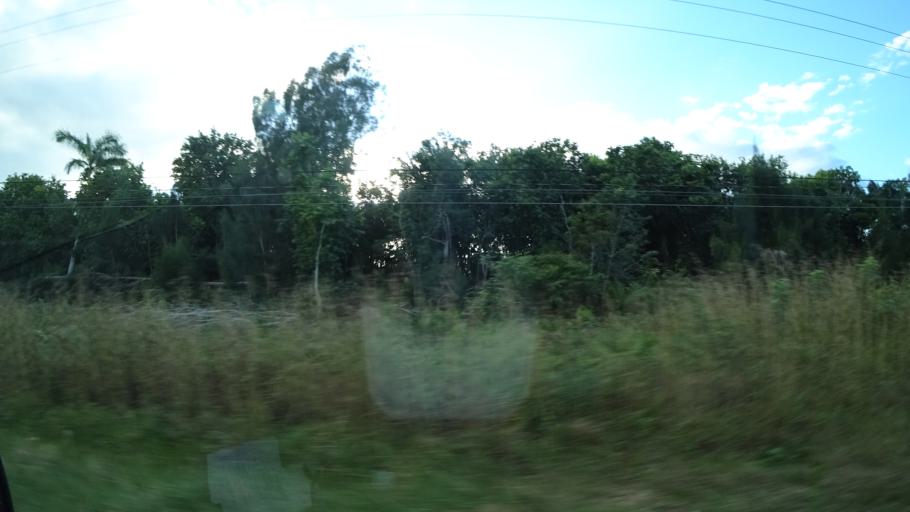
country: BZ
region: Belize
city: Belize City
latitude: 17.5821
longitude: -88.3445
